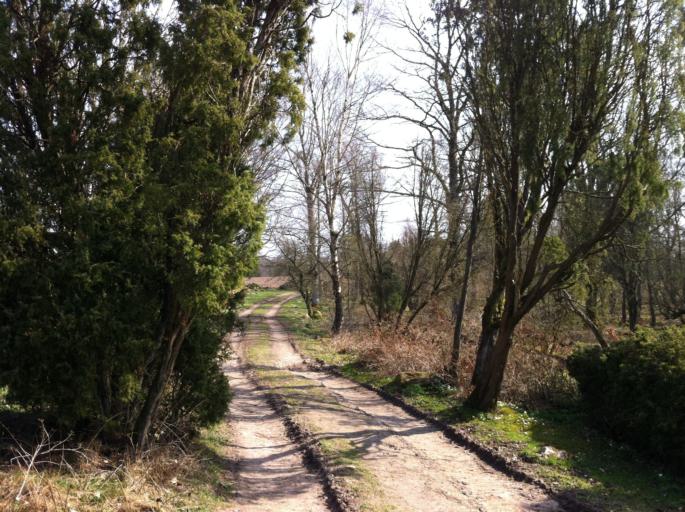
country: SE
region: Skane
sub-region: Eslovs Kommun
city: Stehag
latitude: 56.0094
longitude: 13.3747
